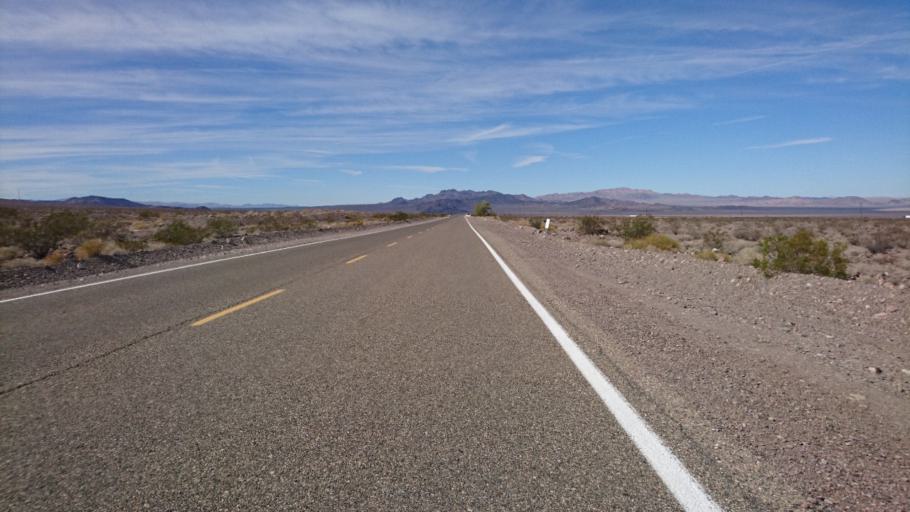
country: US
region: California
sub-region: San Bernardino County
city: Twentynine Palms
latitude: 34.7181
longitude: -116.1106
